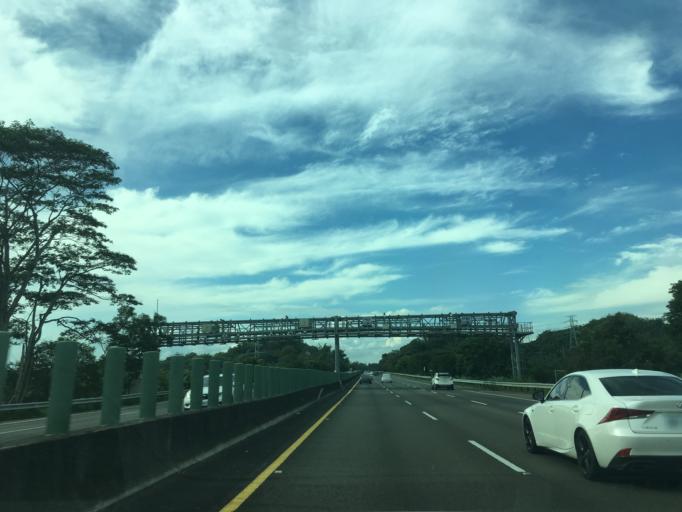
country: TW
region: Taiwan
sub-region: Chiayi
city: Jiayi Shi
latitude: 23.5572
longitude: 120.5050
